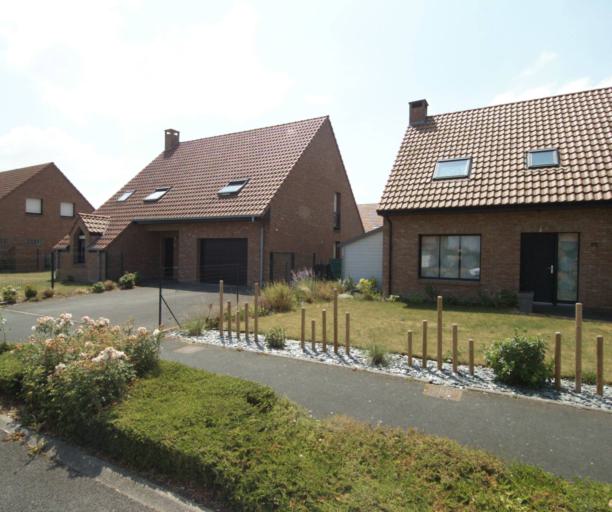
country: FR
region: Nord-Pas-de-Calais
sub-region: Departement du Nord
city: Armentieres
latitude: 50.7000
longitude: 2.8921
